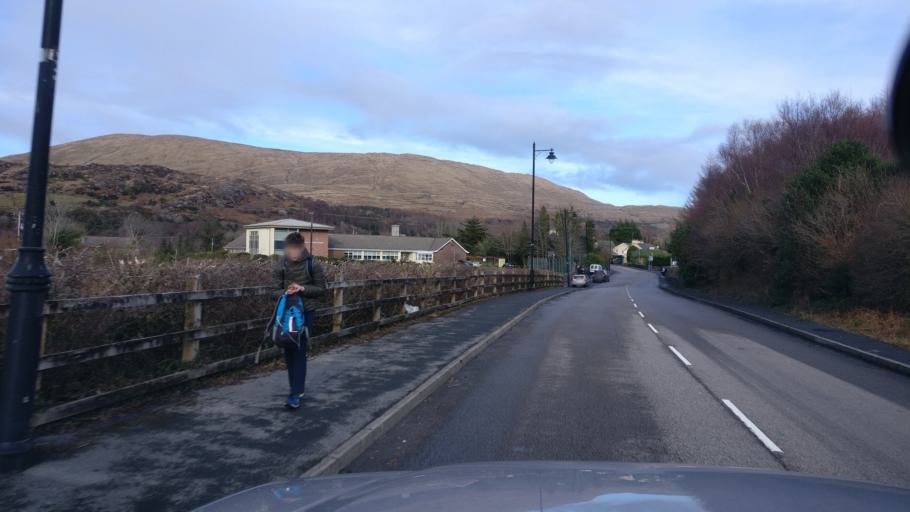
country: IE
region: Connaught
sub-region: County Galway
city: Oughterard
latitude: 53.5128
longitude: -9.4528
